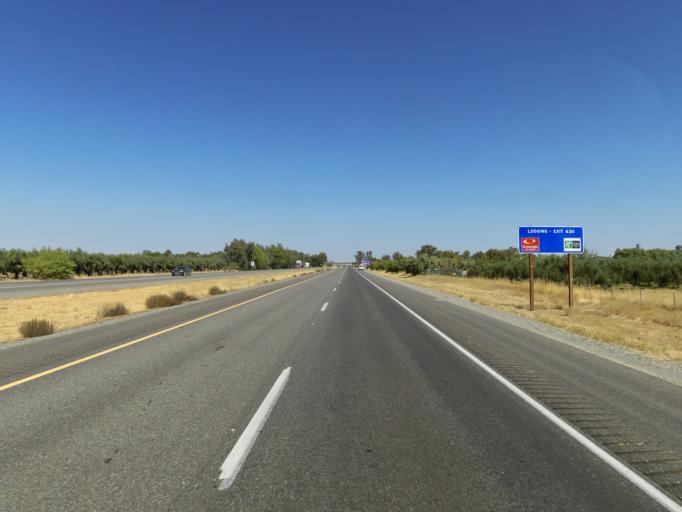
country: US
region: California
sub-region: Tehama County
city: Corning
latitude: 39.8920
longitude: -122.2000
